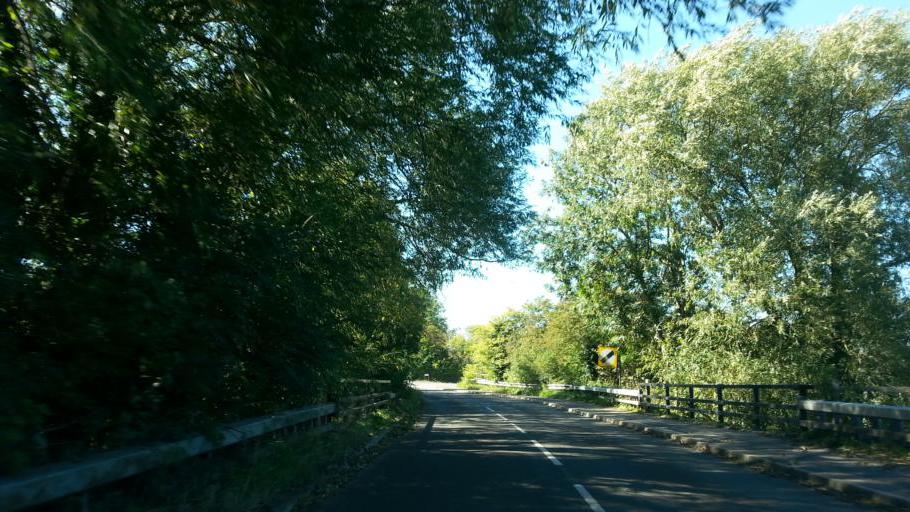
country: GB
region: England
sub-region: Staffordshire
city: Stafford
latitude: 52.8114
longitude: -2.1518
